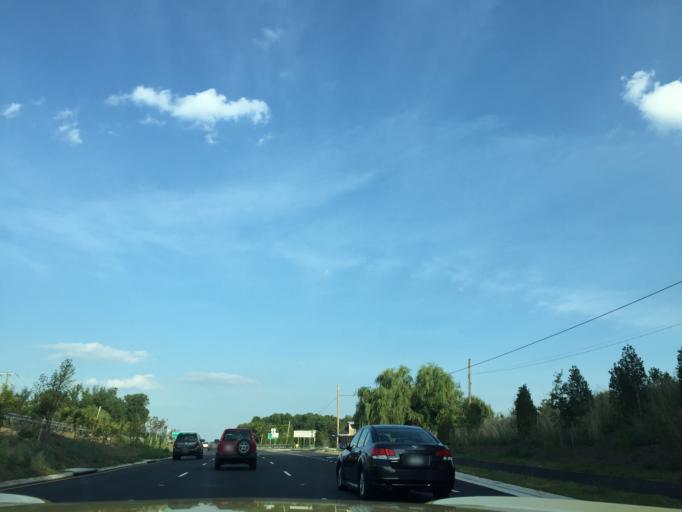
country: US
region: Virginia
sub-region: Fairfax County
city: Dranesville
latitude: 39.0034
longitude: -77.3512
